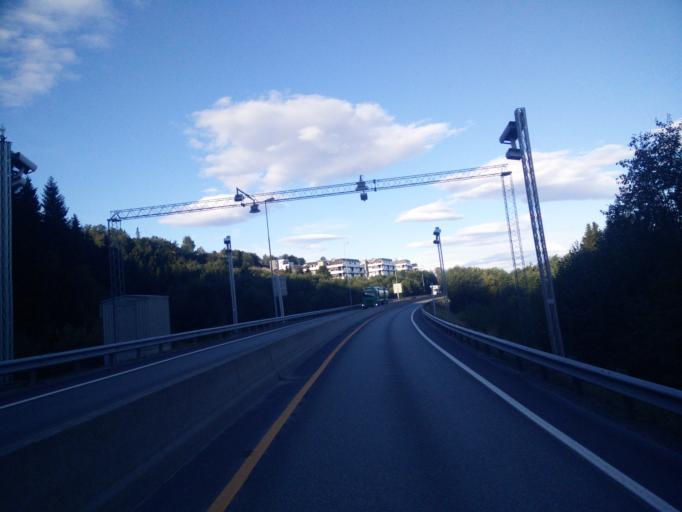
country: NO
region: Sor-Trondelag
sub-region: Malvik
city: Malvik
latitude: 63.4226
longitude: 10.5551
